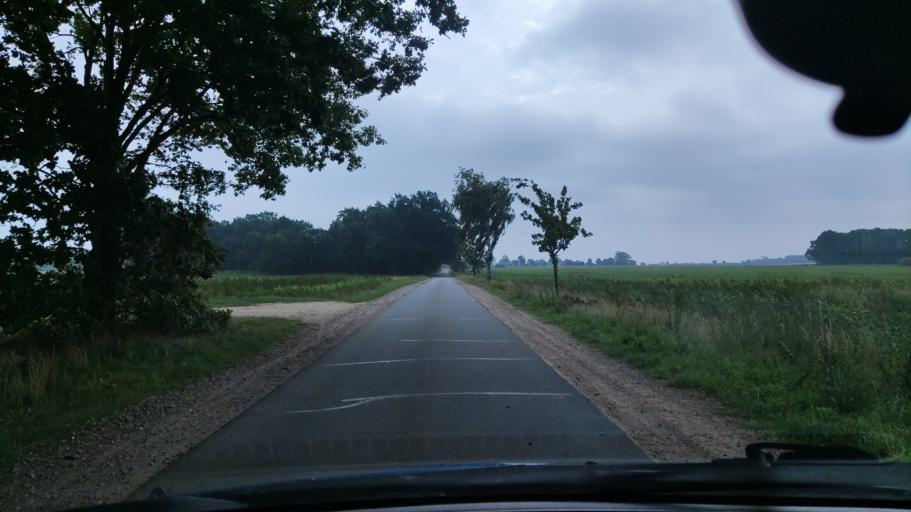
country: DE
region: Lower Saxony
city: Altenmedingen
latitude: 53.1247
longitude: 10.6232
